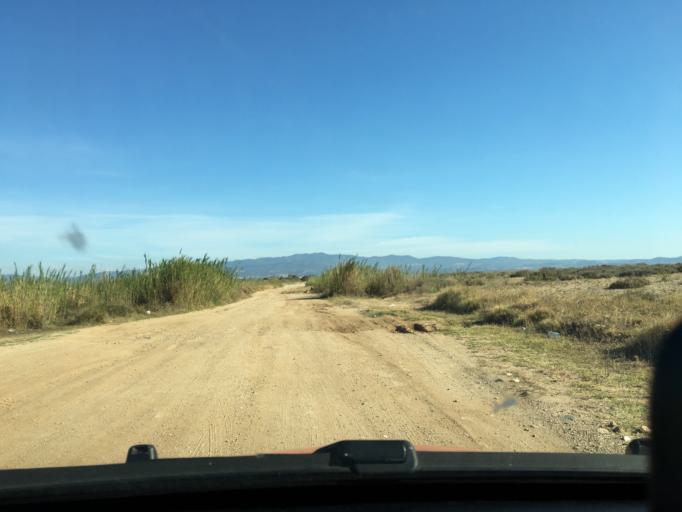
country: GR
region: Central Macedonia
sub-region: Nomos Chalkidikis
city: Nea Potidhaia
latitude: 40.2342
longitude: 23.3431
